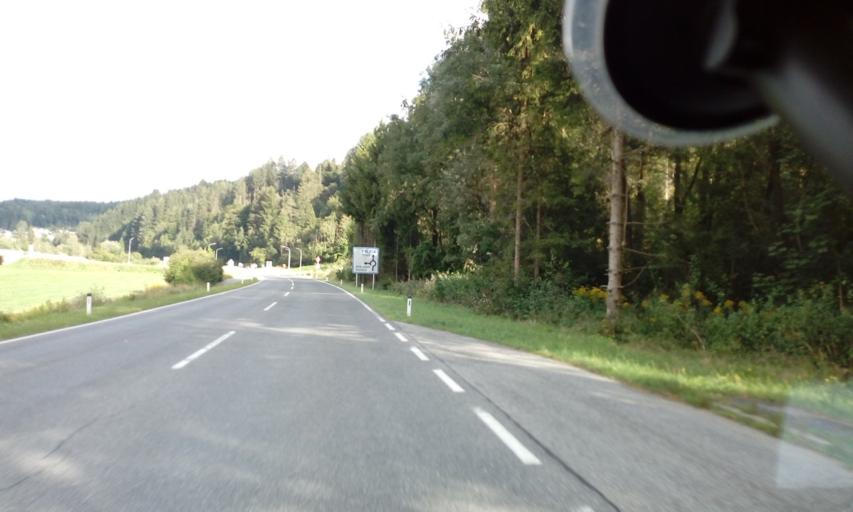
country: AT
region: Carinthia
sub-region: Villach Stadt
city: Villach
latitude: 46.6504
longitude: 13.7692
